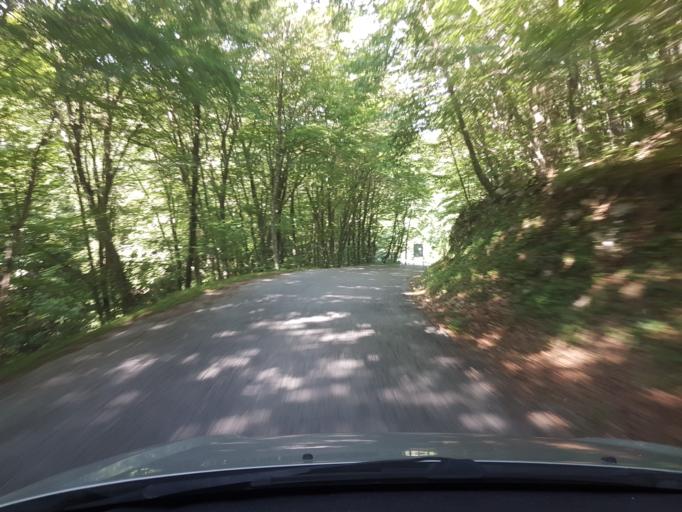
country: SI
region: Divaca
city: Divaca
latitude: 45.7541
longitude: 13.9939
